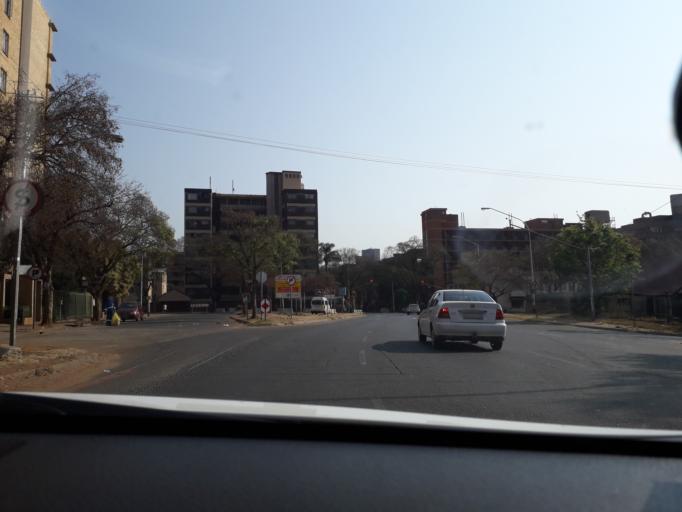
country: ZA
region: Gauteng
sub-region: City of Tshwane Metropolitan Municipality
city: Pretoria
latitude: -25.7574
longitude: 28.1935
